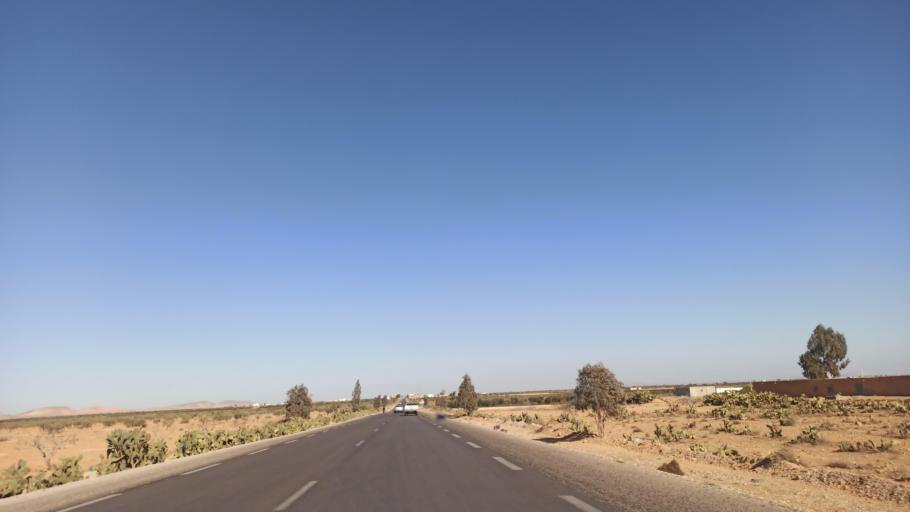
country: TN
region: Sidi Bu Zayd
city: Bi'r al Hufayy
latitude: 34.9583
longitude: 9.2187
